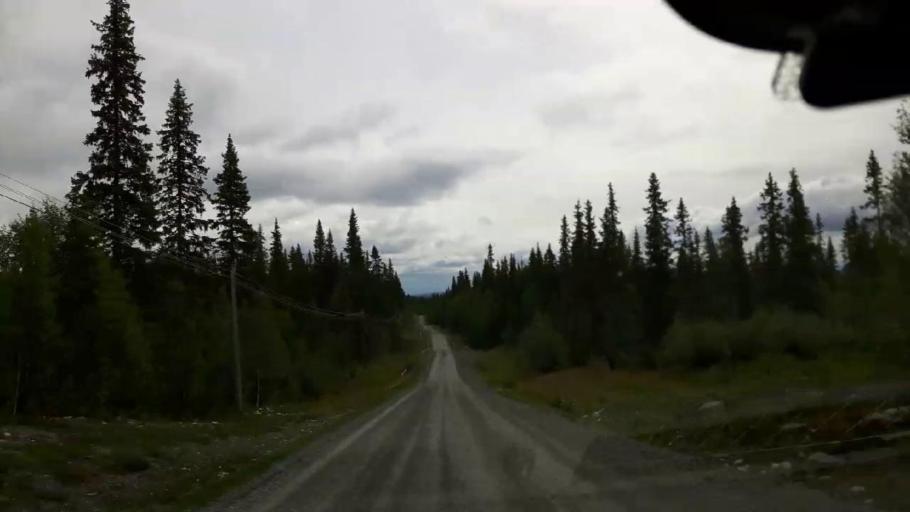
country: SE
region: Jaemtland
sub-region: Krokoms Kommun
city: Valla
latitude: 63.7244
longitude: 13.8473
